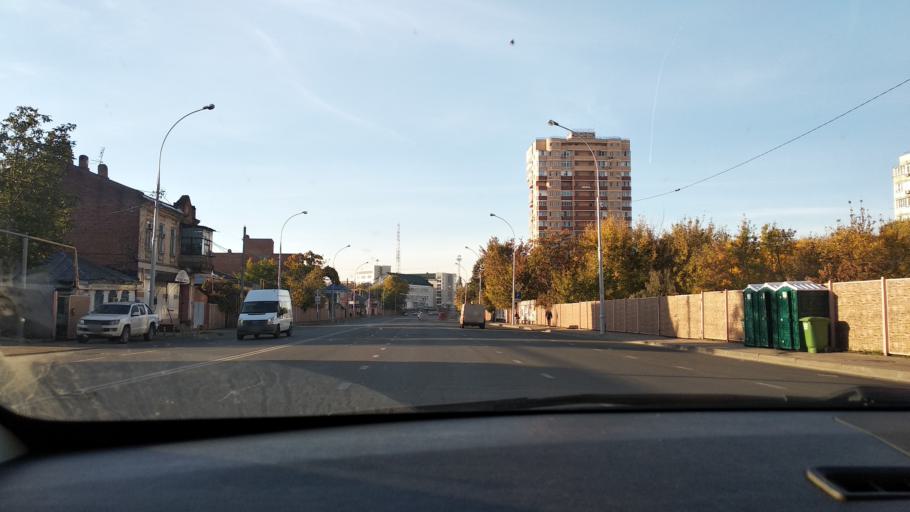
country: RU
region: Krasnodarskiy
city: Krasnodar
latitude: 45.0184
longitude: 38.9806
